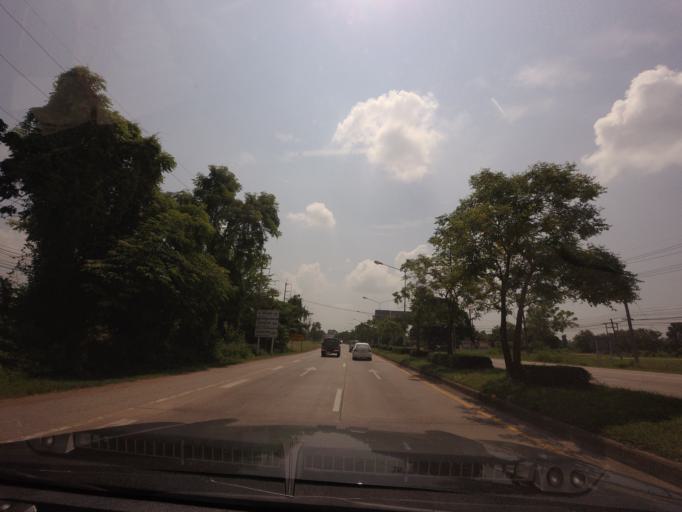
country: TH
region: Uttaradit
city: Uttaradit
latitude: 17.6067
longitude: 100.1233
